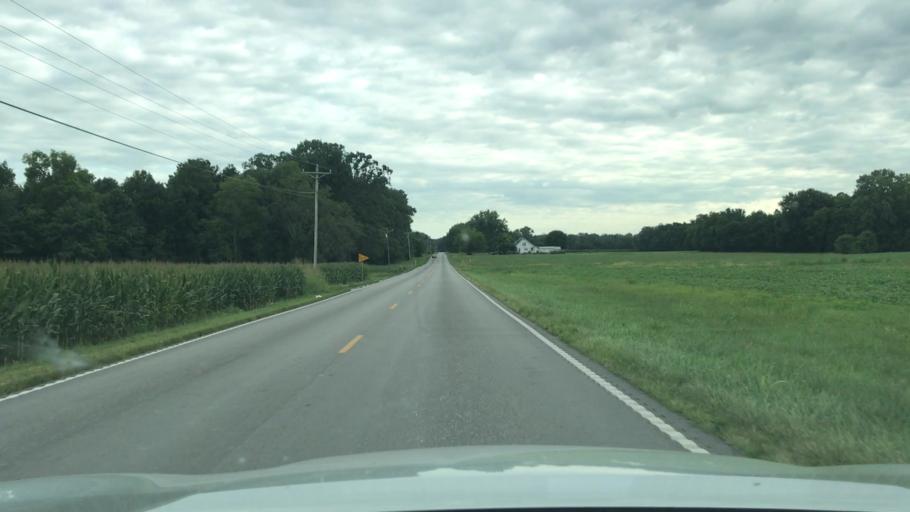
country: US
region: Kentucky
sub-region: Todd County
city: Guthrie
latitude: 36.7128
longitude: -87.1930
